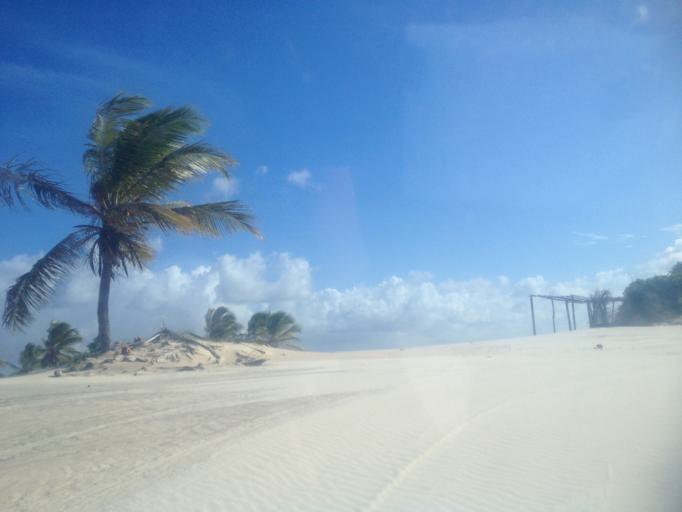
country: BR
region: Sergipe
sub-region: Indiaroba
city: Indiaroba
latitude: -11.4671
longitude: -37.3682
